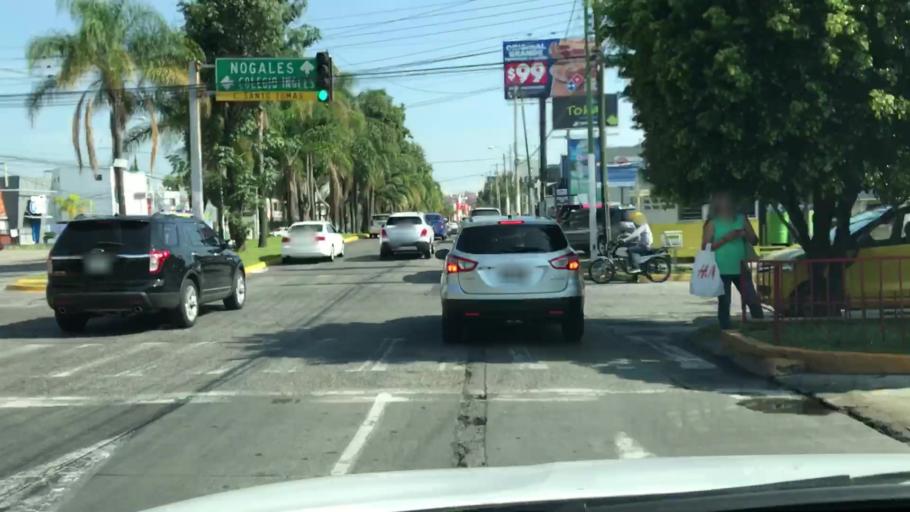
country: MX
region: Jalisco
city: Guadalajara
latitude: 20.6667
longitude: -103.4242
